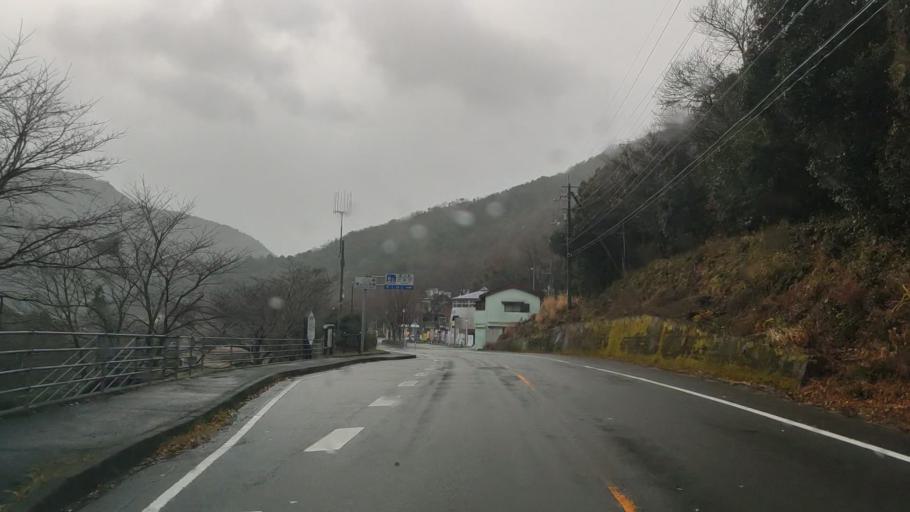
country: JP
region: Tokushima
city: Kamojimacho-jogejima
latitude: 34.1522
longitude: 134.3527
